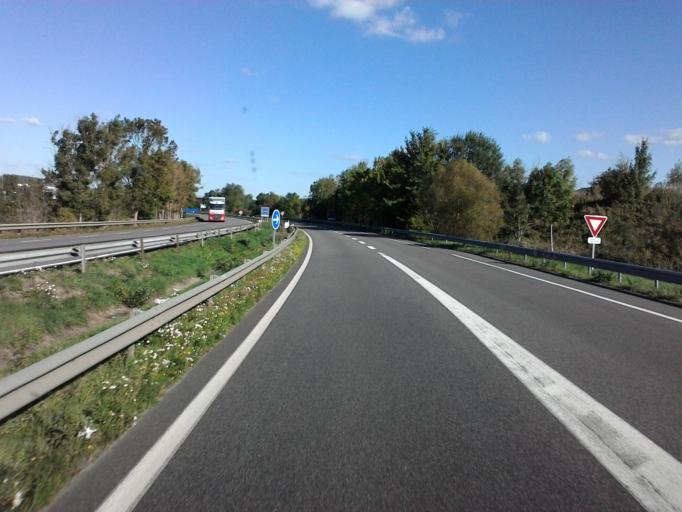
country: FR
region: Lorraine
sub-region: Departement de Meurthe-et-Moselle
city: Mont-Saint-Martin
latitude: 49.5475
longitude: 5.8003
